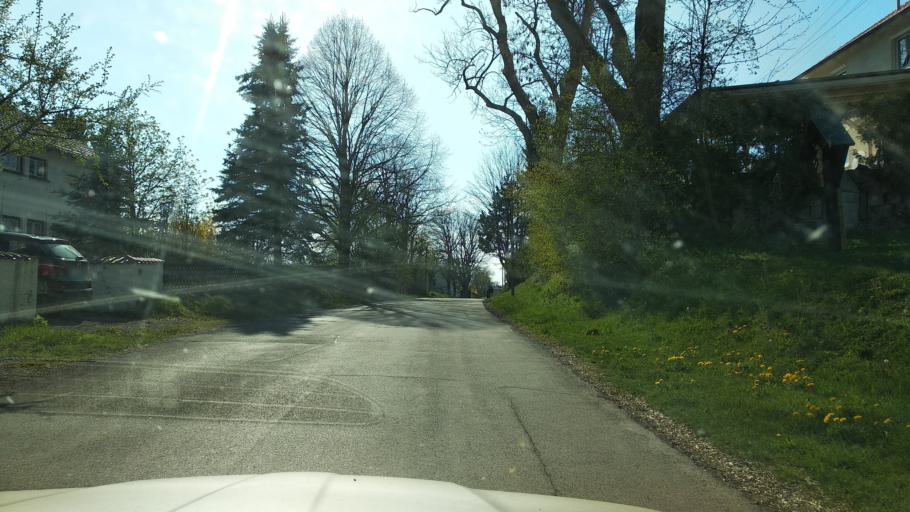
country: DE
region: Bavaria
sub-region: Swabia
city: Hawangen
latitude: 47.9717
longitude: 10.2748
